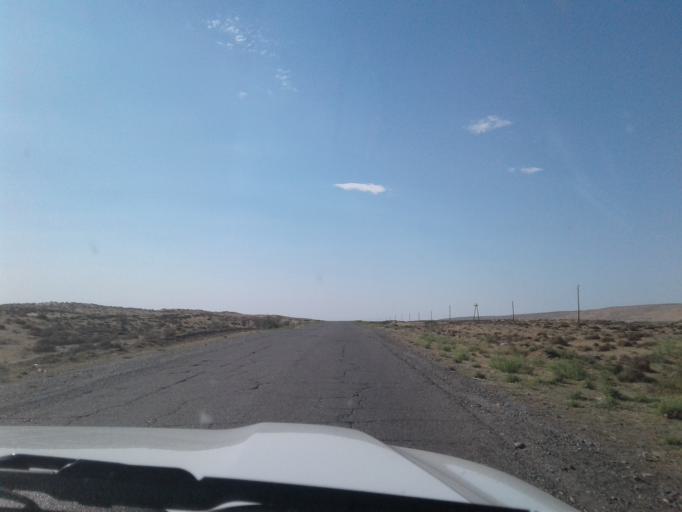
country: TM
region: Mary
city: Yoloeten
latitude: 36.5698
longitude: 62.5371
